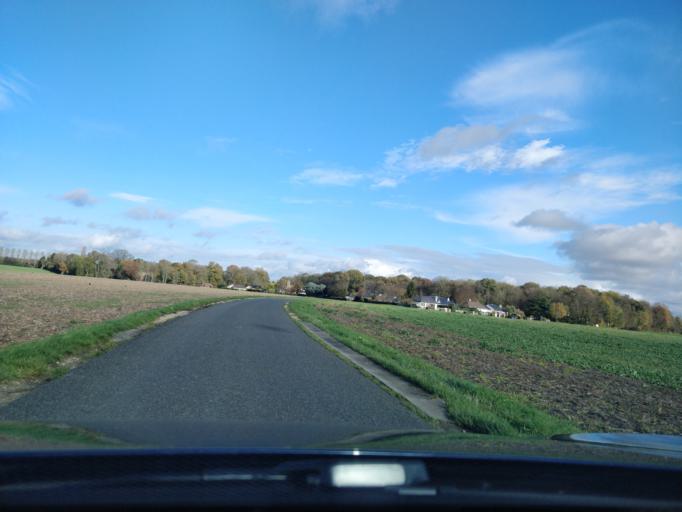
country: FR
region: Ile-de-France
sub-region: Departement de l'Essonne
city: Fontenay-les-Briis
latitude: 48.6421
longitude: 2.1485
